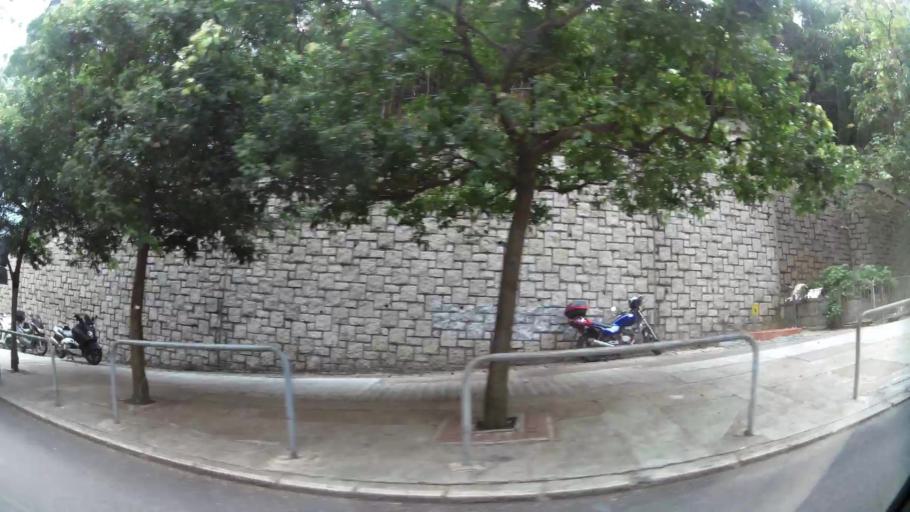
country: HK
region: Wanchai
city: Wan Chai
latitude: 22.2619
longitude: 114.2352
